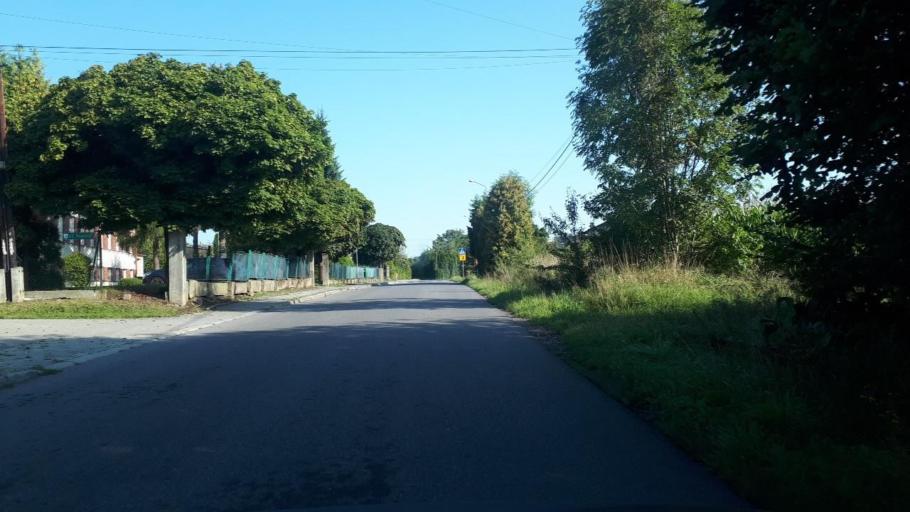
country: PL
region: Silesian Voivodeship
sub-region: Powiat cieszynski
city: Chybie
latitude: 49.8696
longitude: 18.8569
